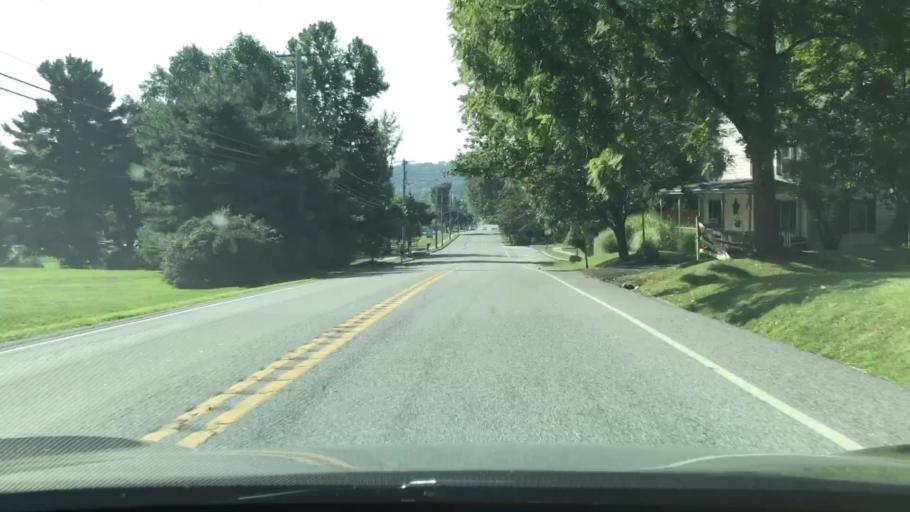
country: US
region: Pennsylvania
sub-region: Montgomery County
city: Dresher
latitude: 40.1472
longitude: -75.1695
